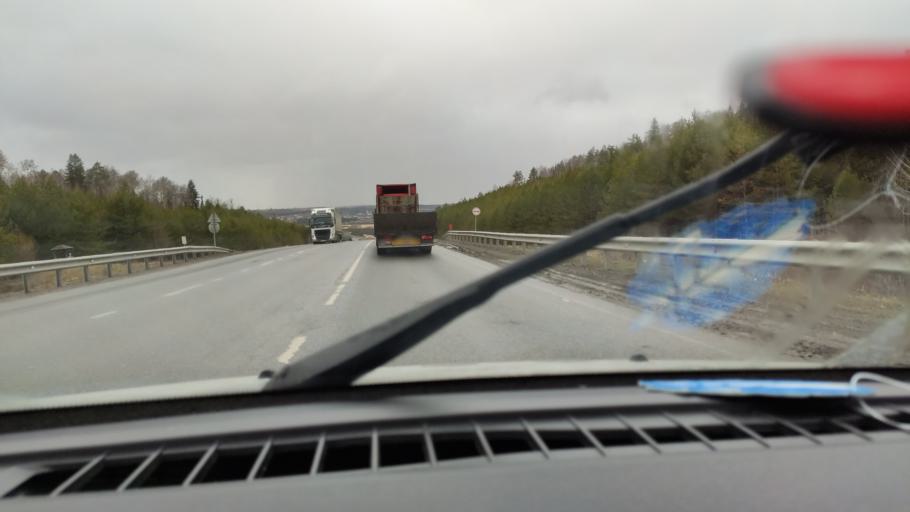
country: RU
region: Perm
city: Kungur
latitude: 57.3507
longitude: 56.9368
